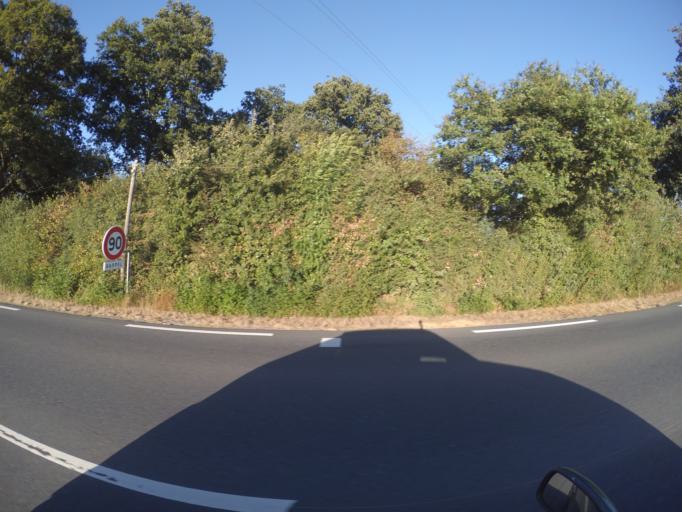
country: FR
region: Pays de la Loire
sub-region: Departement de la Loire-Atlantique
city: Remouille
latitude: 47.0476
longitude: -1.3645
